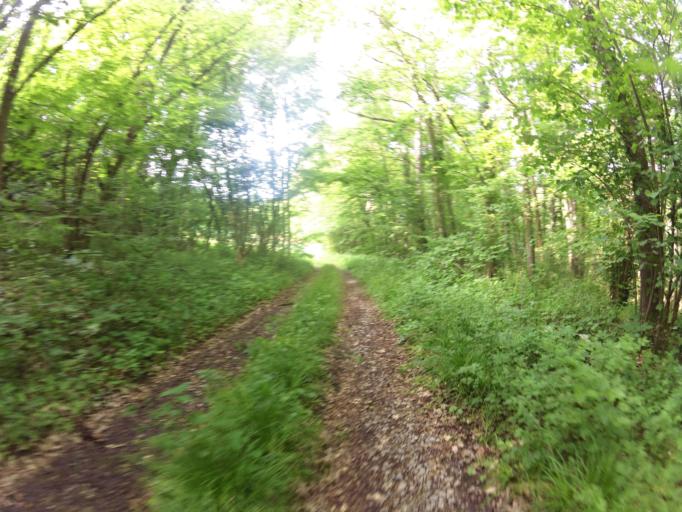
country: DE
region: Bavaria
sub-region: Regierungsbezirk Unterfranken
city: Frickenhausen
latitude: 49.6790
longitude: 10.0763
